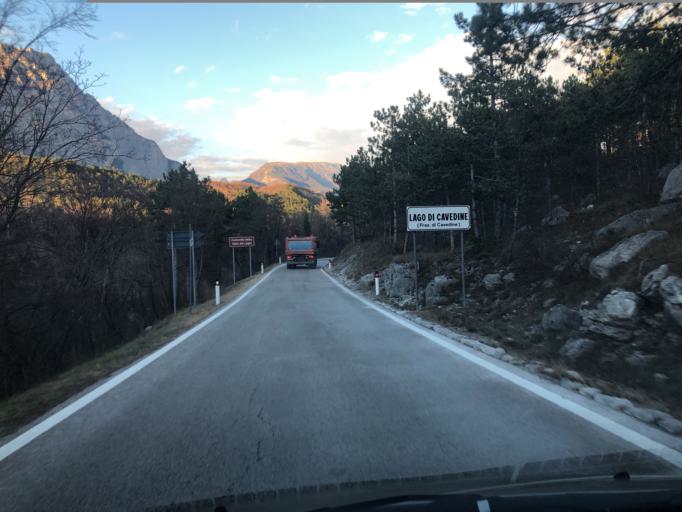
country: IT
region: Trentino-Alto Adige
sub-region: Provincia di Trento
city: Drena
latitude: 45.9907
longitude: 10.9427
